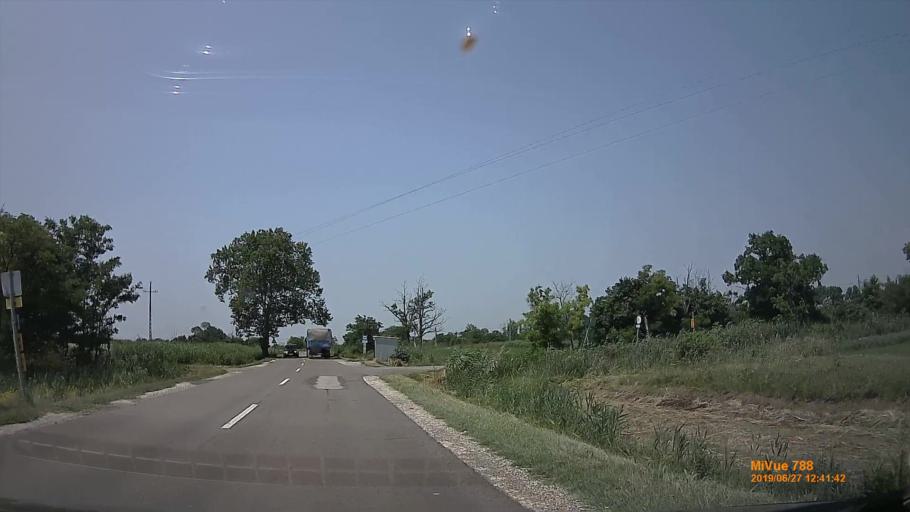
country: HU
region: Pest
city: Tortel
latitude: 47.1815
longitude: 19.8935
